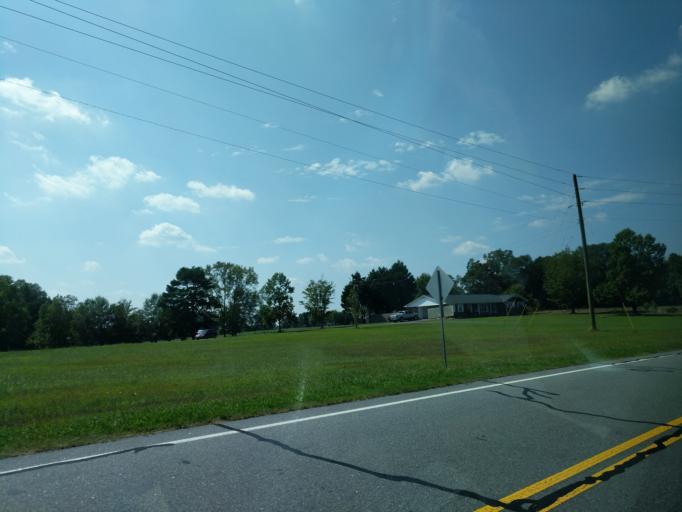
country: US
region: Georgia
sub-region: Hart County
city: Hartwell
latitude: 34.3894
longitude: -83.0214
